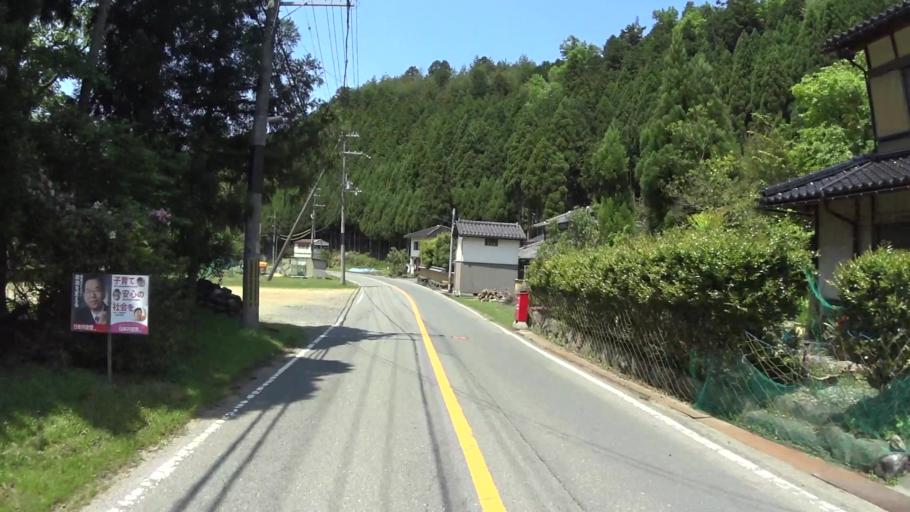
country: JP
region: Kyoto
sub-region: Kyoto-shi
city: Kamigyo-ku
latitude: 35.1990
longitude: 135.6905
